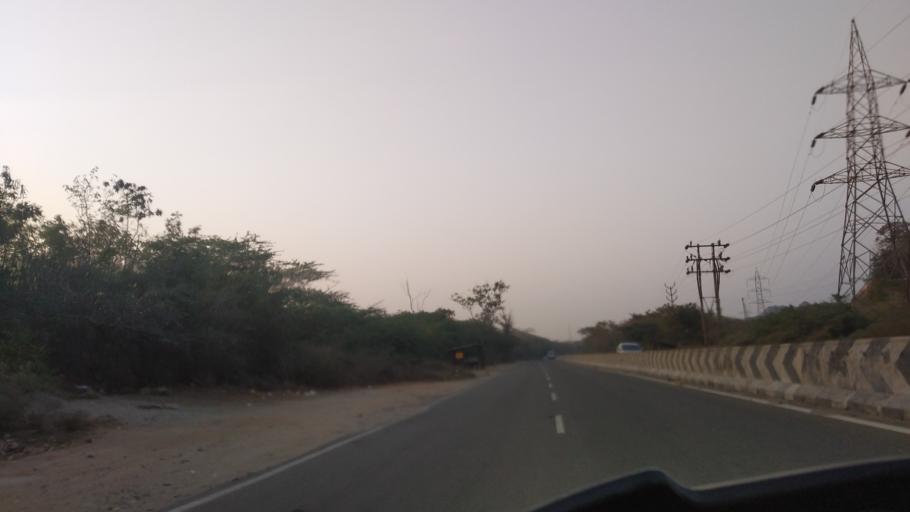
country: IN
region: Tamil Nadu
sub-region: Coimbatore
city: Madukkarai
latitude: 10.9242
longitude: 76.9492
